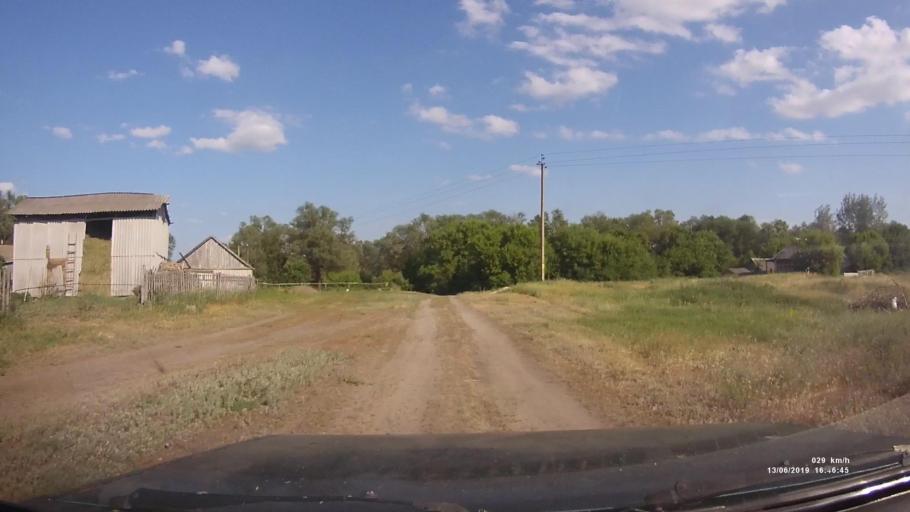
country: RU
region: Rostov
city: Kazanskaya
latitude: 49.9448
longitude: 41.4289
